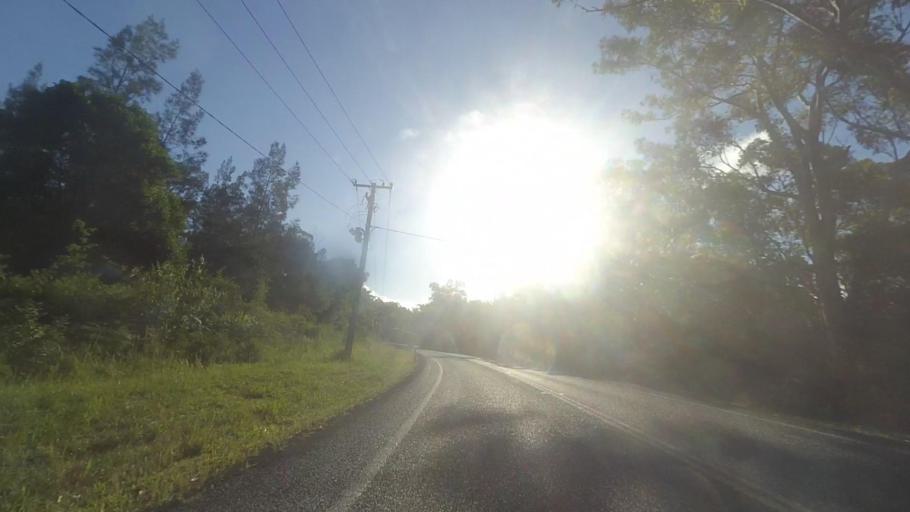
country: AU
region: New South Wales
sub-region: Great Lakes
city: Nabiac
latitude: -32.0895
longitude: 152.4628
